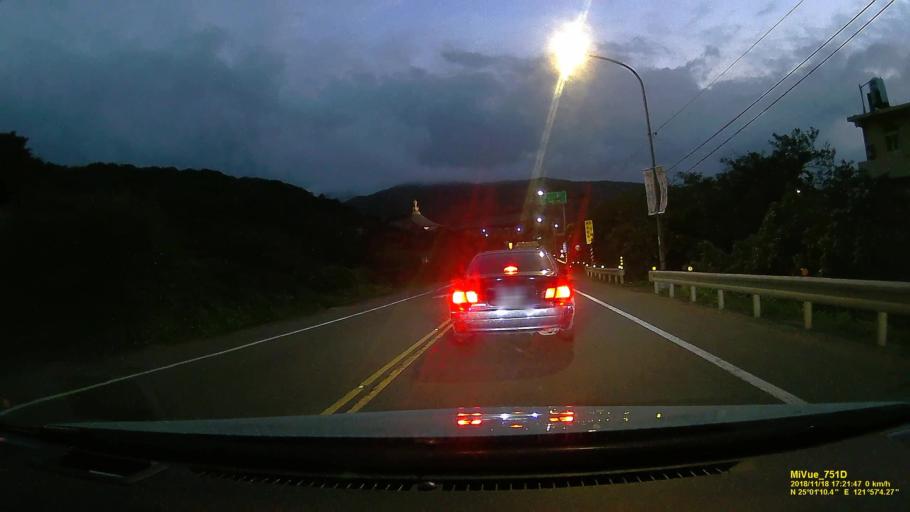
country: TW
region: Taiwan
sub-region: Keelung
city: Keelung
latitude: 25.0195
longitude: 121.9511
